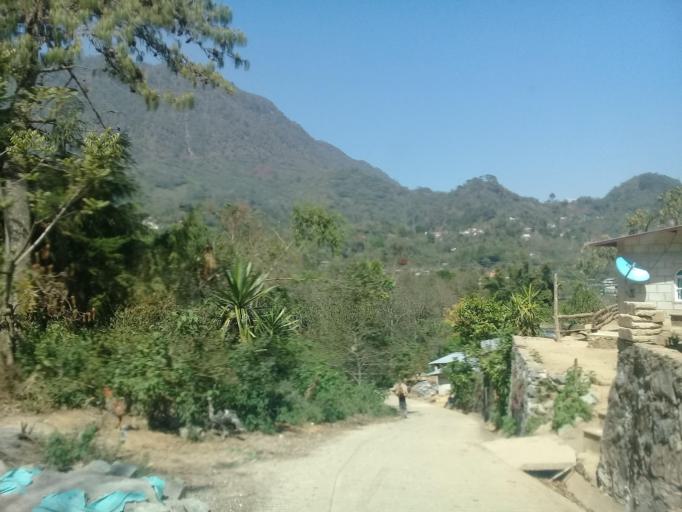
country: MX
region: Veracruz
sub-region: Tlilapan
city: Tonalixco
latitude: 18.7589
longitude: -97.0403
